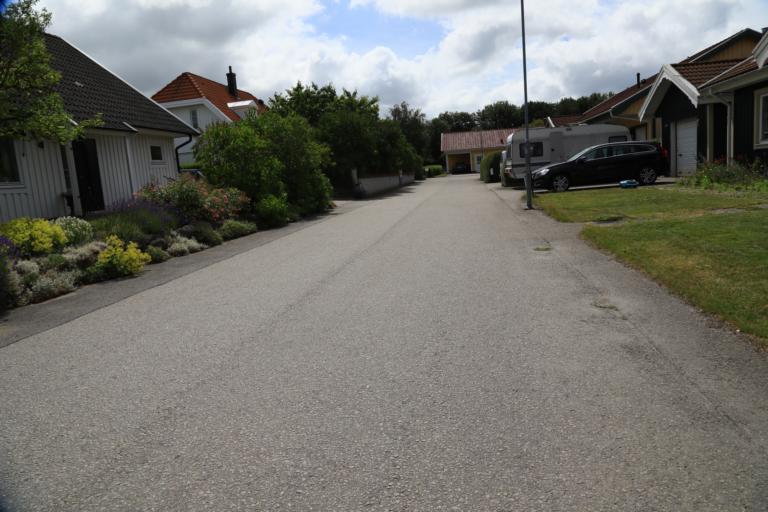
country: SE
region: Halland
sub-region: Varbergs Kommun
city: Varberg
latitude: 57.1123
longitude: 12.2944
